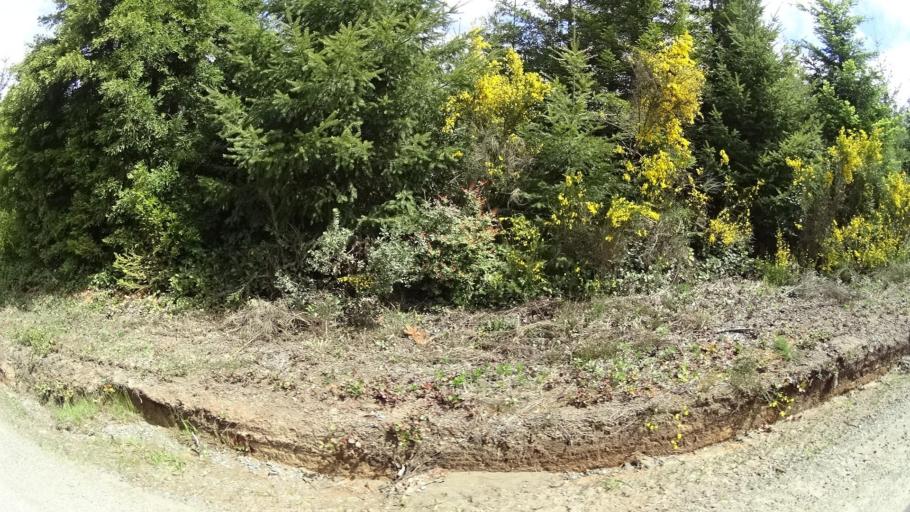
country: US
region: California
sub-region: Humboldt County
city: Blue Lake
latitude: 40.7728
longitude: -123.9621
